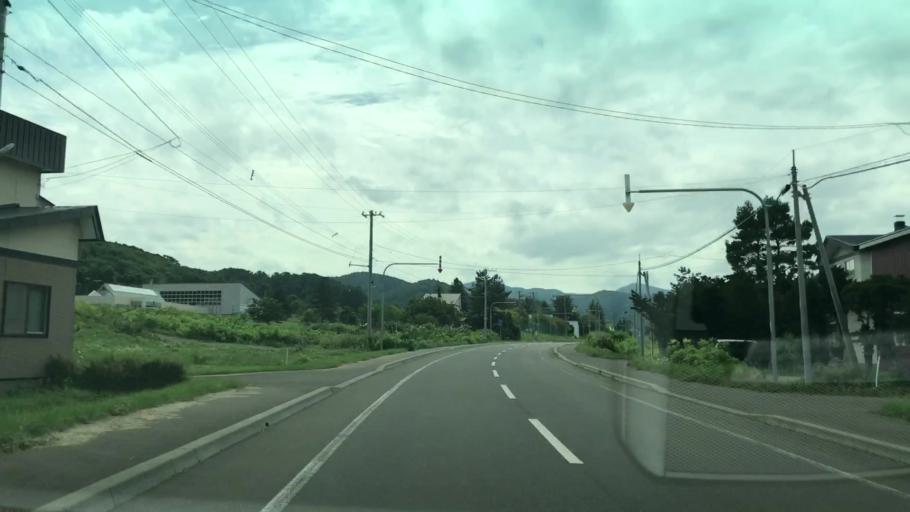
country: JP
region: Hokkaido
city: Yoichi
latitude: 43.1833
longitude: 140.8445
